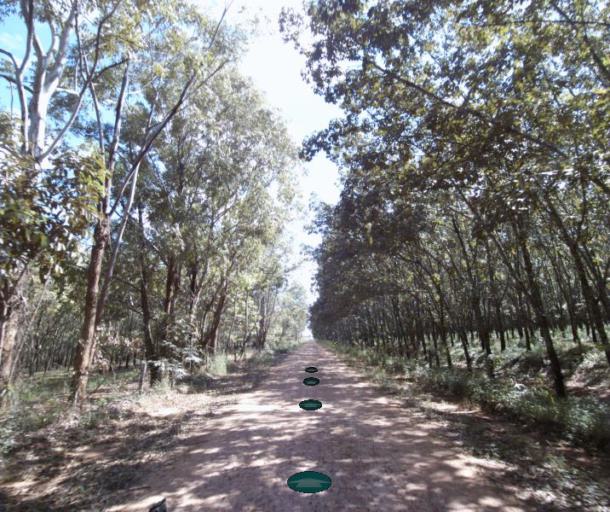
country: BR
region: Goias
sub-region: Pirenopolis
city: Pirenopolis
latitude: -15.7773
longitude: -49.0357
